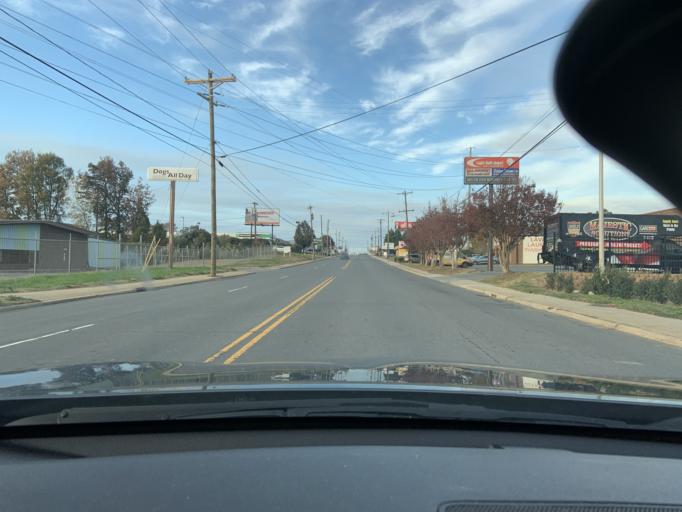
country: US
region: North Carolina
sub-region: Mecklenburg County
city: Charlotte
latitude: 35.1842
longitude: -80.8757
